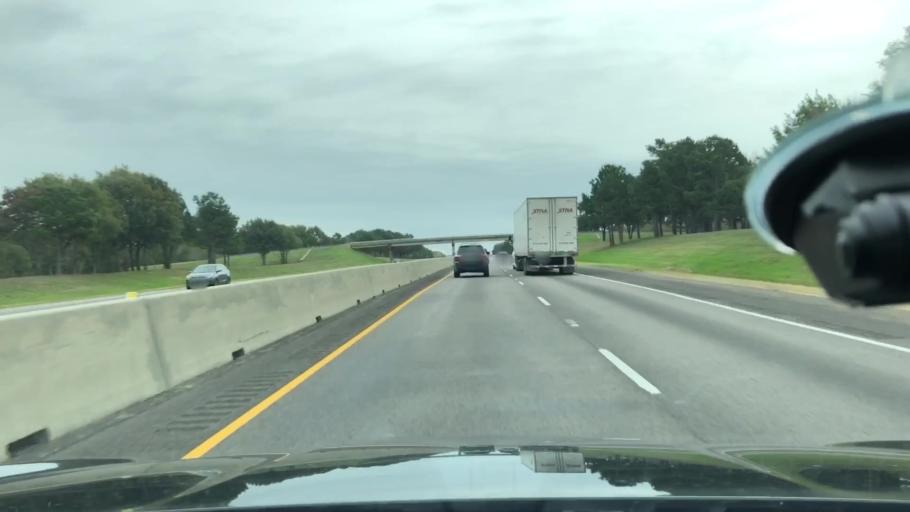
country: US
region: Texas
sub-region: Franklin County
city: Mount Vernon
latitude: 33.1661
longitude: -95.3838
